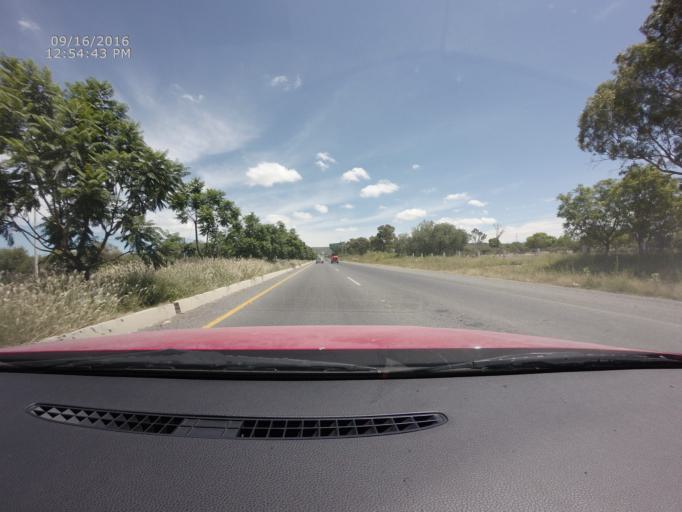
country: MX
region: Queretaro
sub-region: Colon
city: Purisima de Cubos (La Purisima)
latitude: 20.6344
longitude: -100.1155
